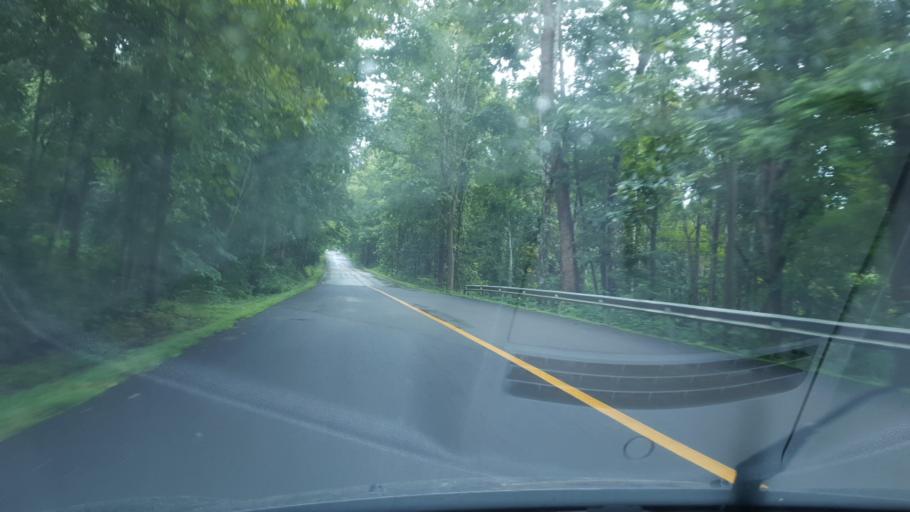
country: TH
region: Mae Hong Son
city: Pa Pae
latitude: 18.2565
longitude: 97.9416
